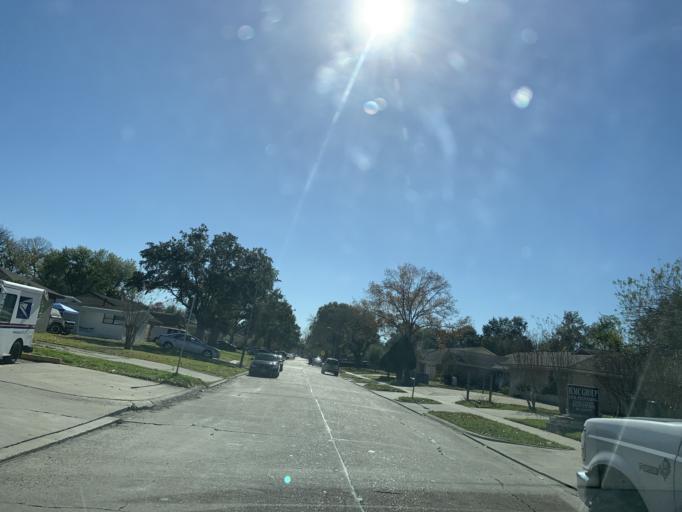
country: US
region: Texas
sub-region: Harris County
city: Bellaire
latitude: 29.6884
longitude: -95.5037
